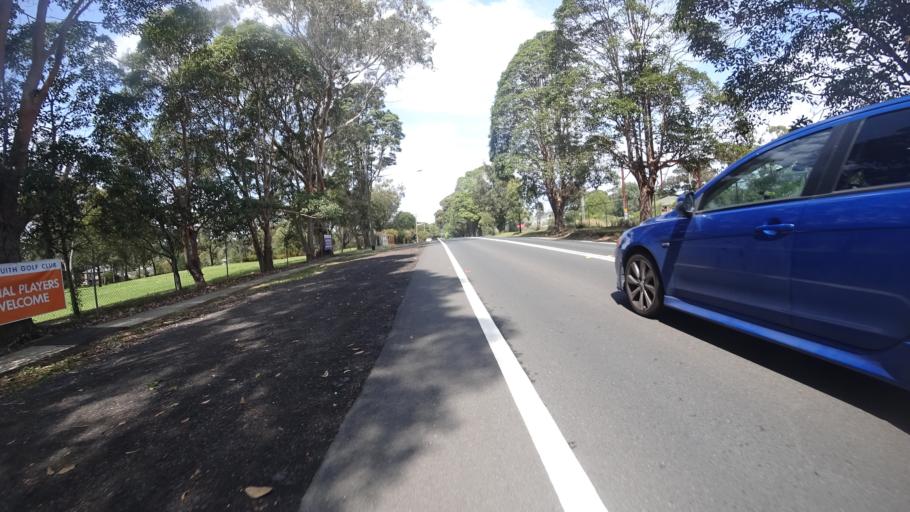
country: AU
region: New South Wales
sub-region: Hornsby Shire
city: Mount Colah
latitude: -33.6818
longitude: 151.1118
